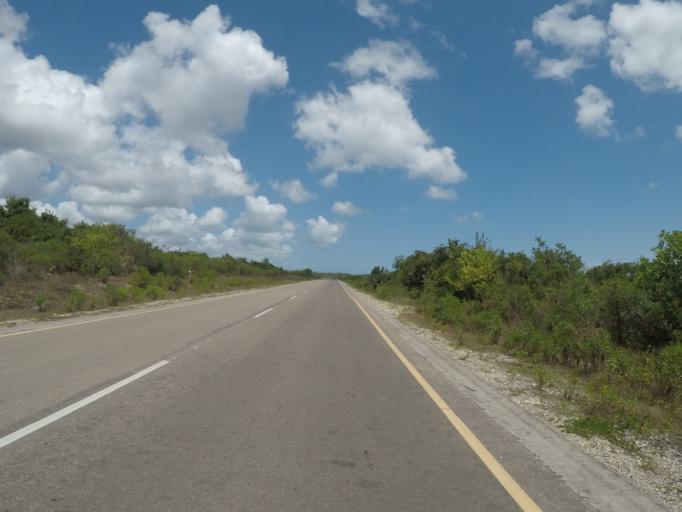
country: TZ
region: Zanzibar Central/South
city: Koani
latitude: -6.2735
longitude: 39.3639
